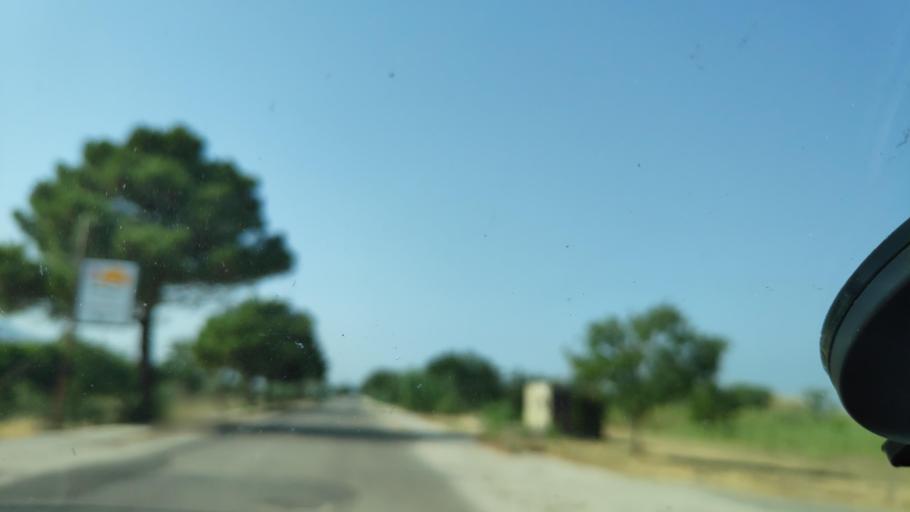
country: IT
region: Calabria
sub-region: Provincia di Catanzaro
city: Badolato Marina
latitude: 38.5734
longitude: 16.5688
